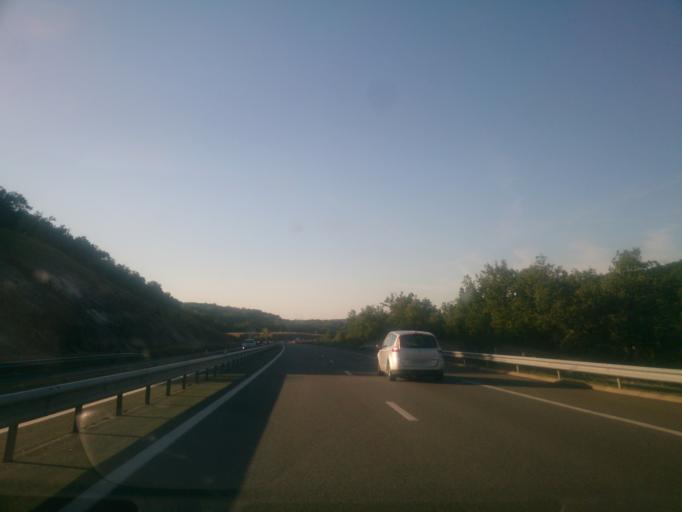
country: FR
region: Midi-Pyrenees
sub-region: Departement du Lot
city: Le Vigan
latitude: 44.7756
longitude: 1.5360
